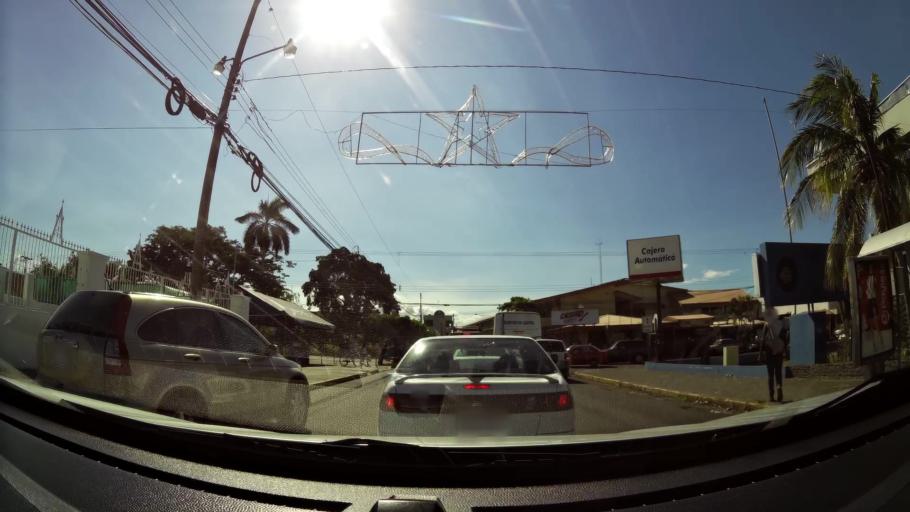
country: CR
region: Guanacaste
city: Liberia
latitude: 10.6303
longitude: -85.4378
